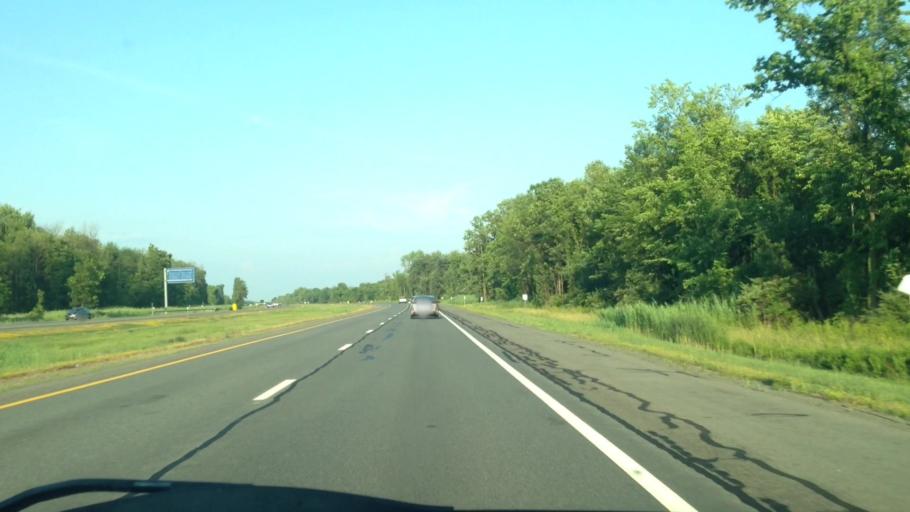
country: US
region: New York
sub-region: Madison County
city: Chittenango
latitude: 43.0950
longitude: -75.8337
